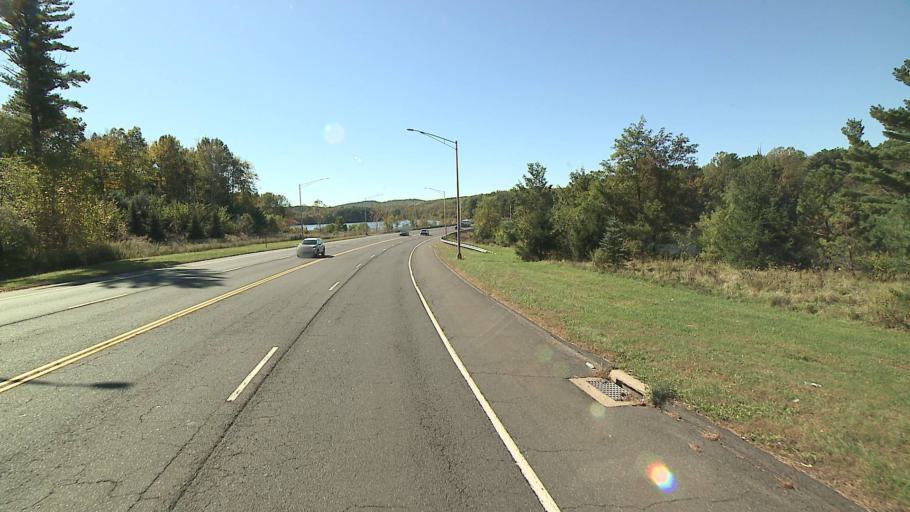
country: US
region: Connecticut
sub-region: Middlesex County
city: Durham
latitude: 41.5402
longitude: -72.7195
